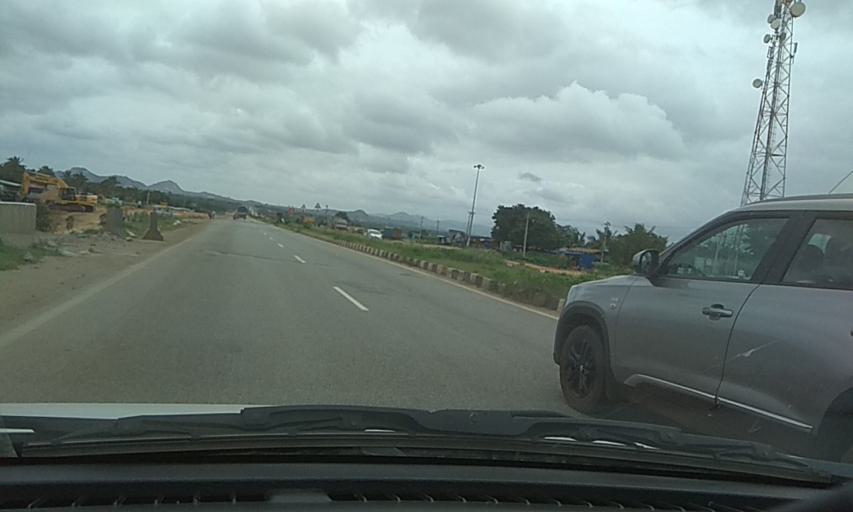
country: IN
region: Karnataka
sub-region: Chitradurga
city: Chitradurga
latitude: 14.2808
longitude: 76.3073
